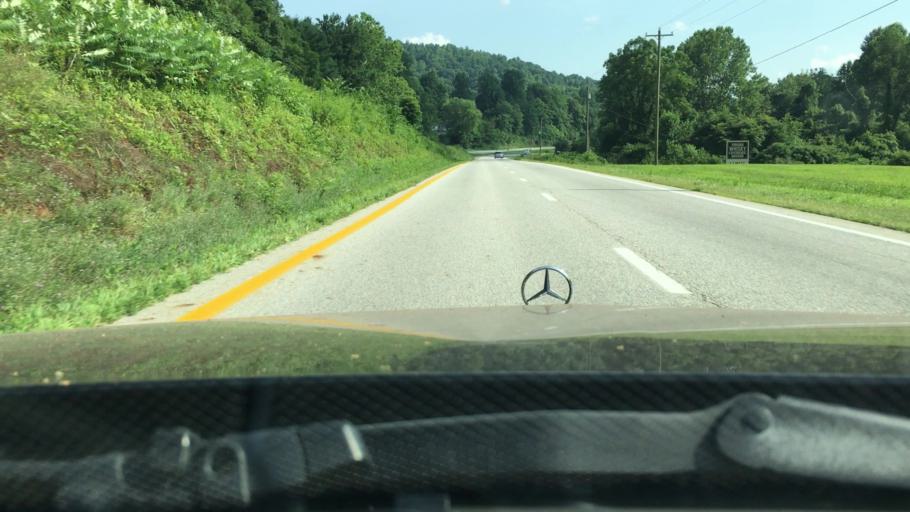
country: US
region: Virginia
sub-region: Nelson County
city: Lovingston
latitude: 37.8000
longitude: -78.8622
